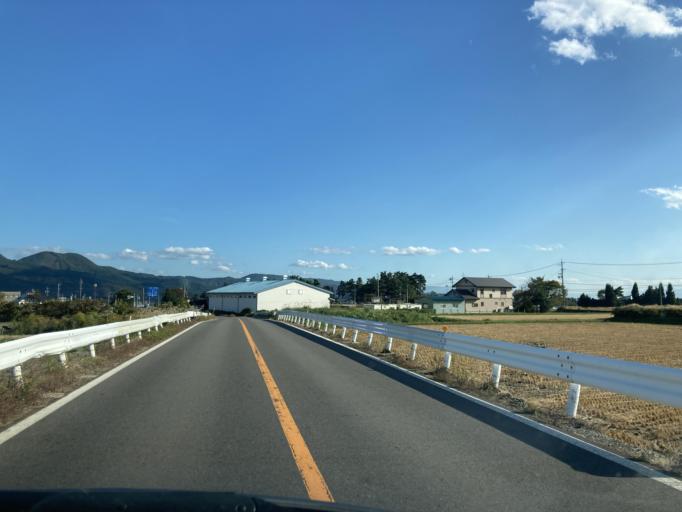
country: JP
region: Nagano
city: Omachi
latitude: 36.5251
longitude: 137.8318
